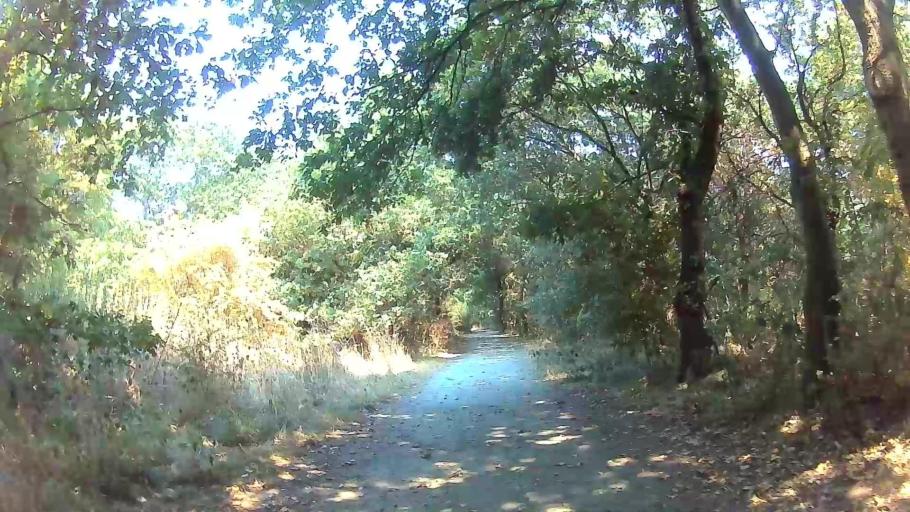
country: GB
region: England
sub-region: Greater London
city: Hornchurch
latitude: 51.5431
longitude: 0.2157
